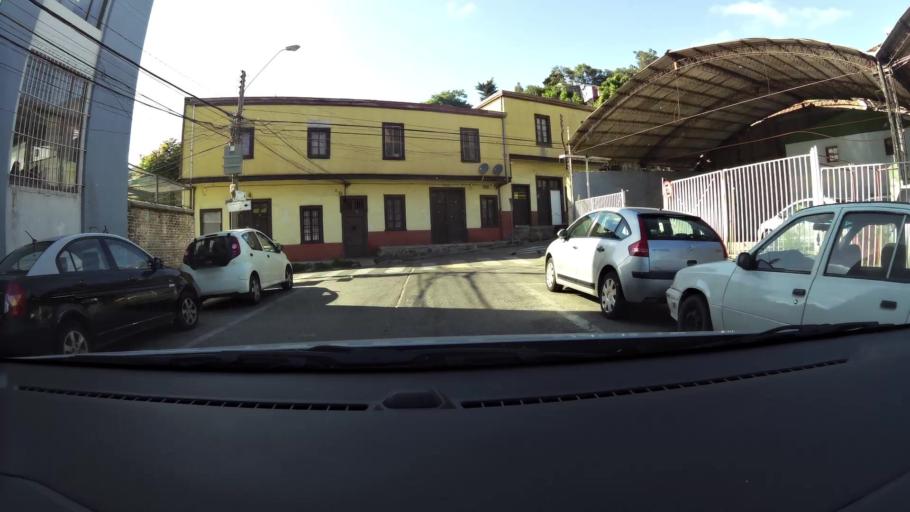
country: CL
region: Valparaiso
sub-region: Provincia de Valparaiso
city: Valparaiso
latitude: -33.0527
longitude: -71.6032
